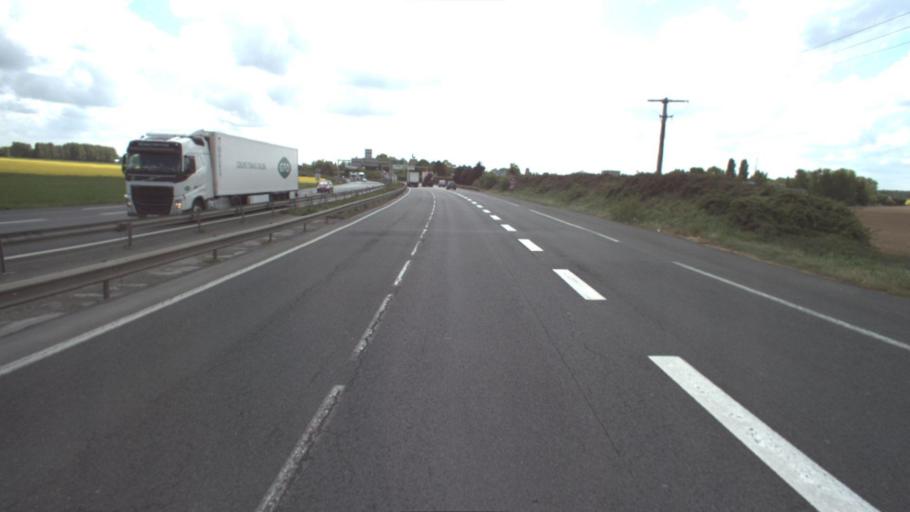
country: FR
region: Ile-de-France
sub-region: Departement de Seine-et-Marne
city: Fontenay-Tresigny
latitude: 48.7147
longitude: 2.8521
